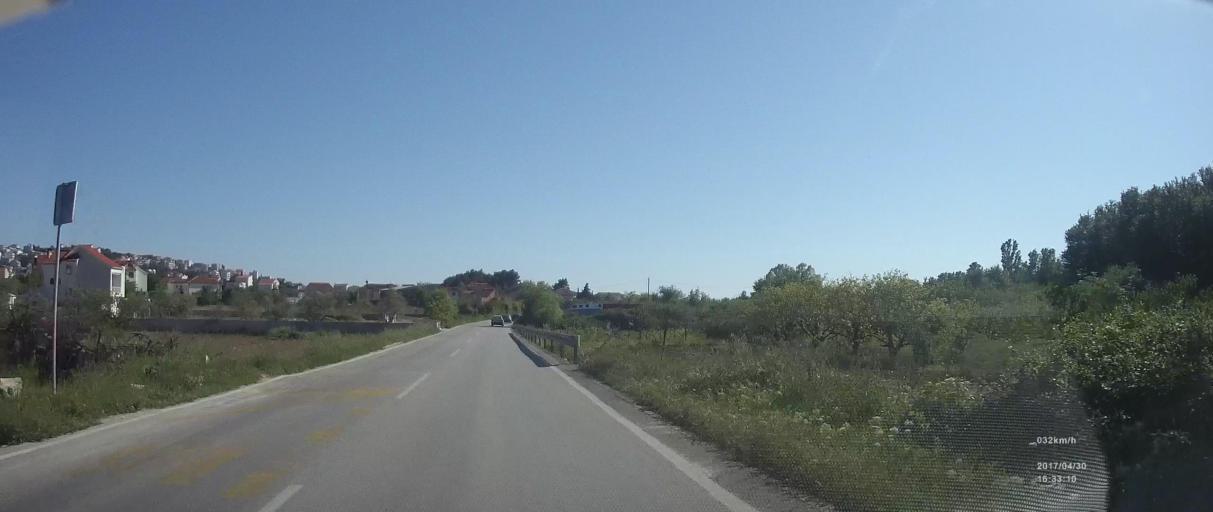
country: HR
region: Splitsko-Dalmatinska
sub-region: Grad Split
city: Stobrec
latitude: 43.5094
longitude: 16.5381
